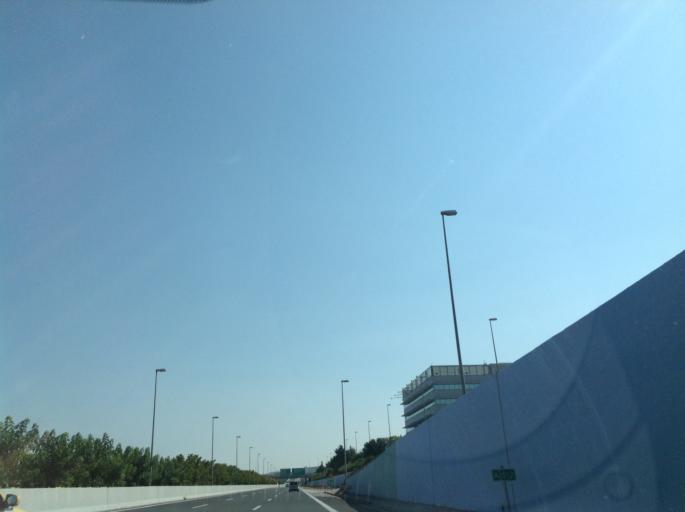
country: GR
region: Attica
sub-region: Nomarchia Anatolikis Attikis
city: Markopoulo
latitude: 37.9234
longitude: 23.9323
